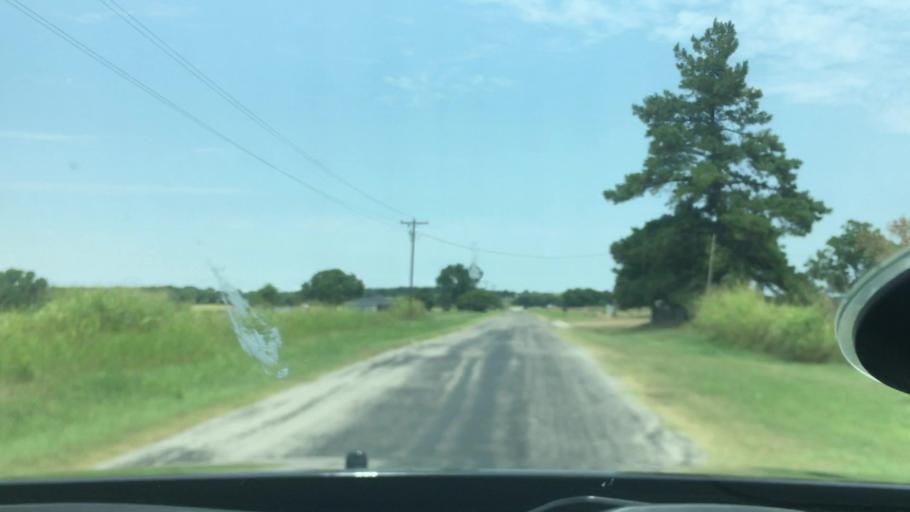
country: US
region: Texas
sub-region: Cooke County
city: Muenster
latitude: 33.8723
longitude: -97.3565
